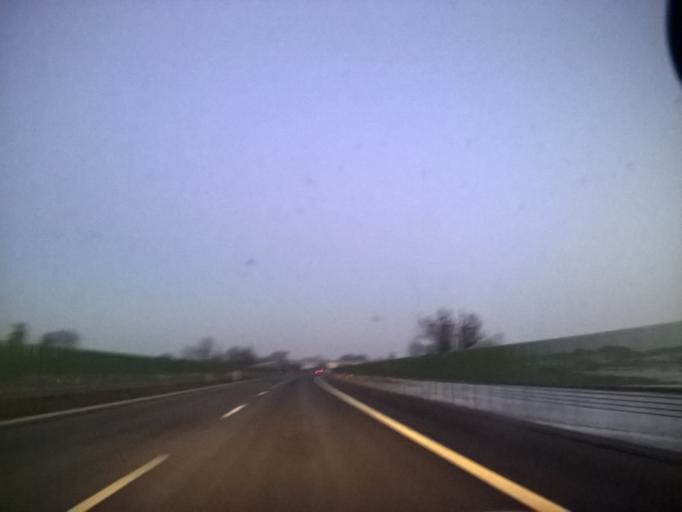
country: PL
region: Warmian-Masurian Voivodeship
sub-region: Powiat olsztynski
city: Biskupiec
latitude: 53.8409
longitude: 21.0096
